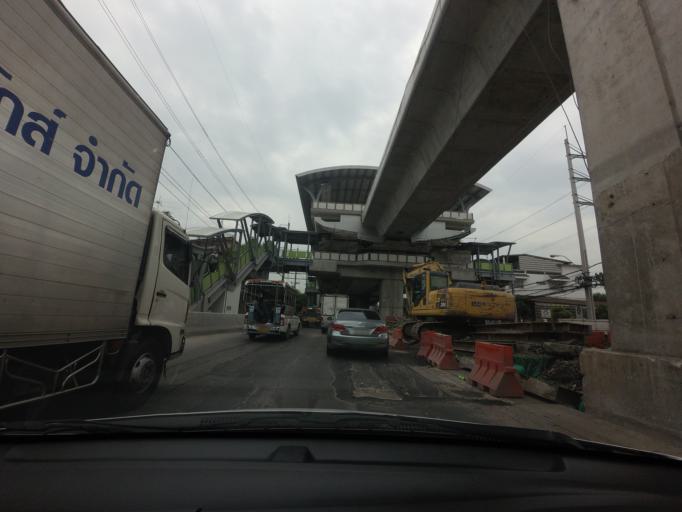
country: TH
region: Samut Prakan
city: Samut Prakan
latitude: 13.5930
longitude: 100.6085
